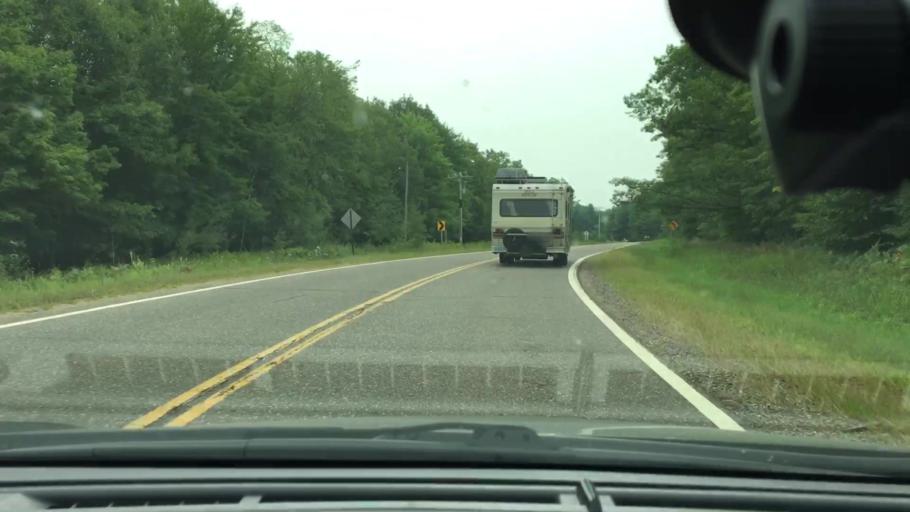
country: US
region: Minnesota
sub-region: Aitkin County
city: Aitkin
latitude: 46.4064
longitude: -93.8083
